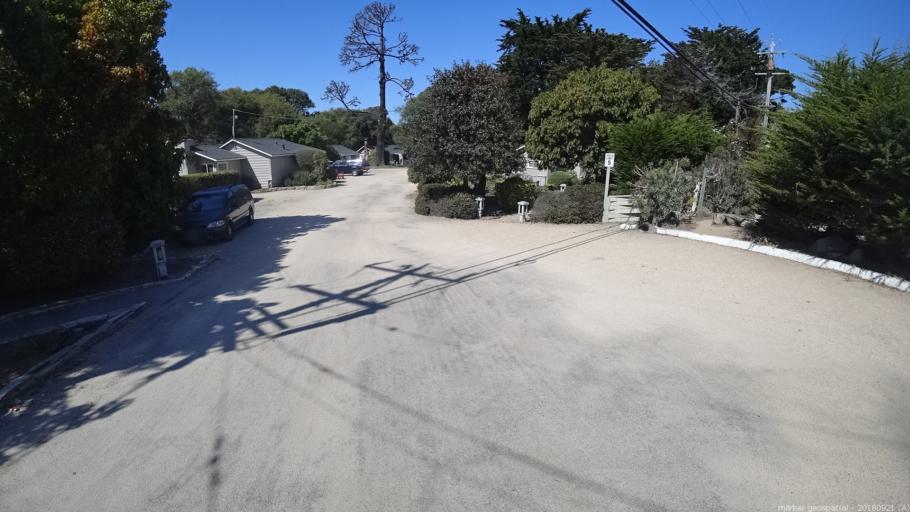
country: US
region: California
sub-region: Monterey County
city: Carmel-by-the-Sea
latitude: 36.5373
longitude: -121.9130
